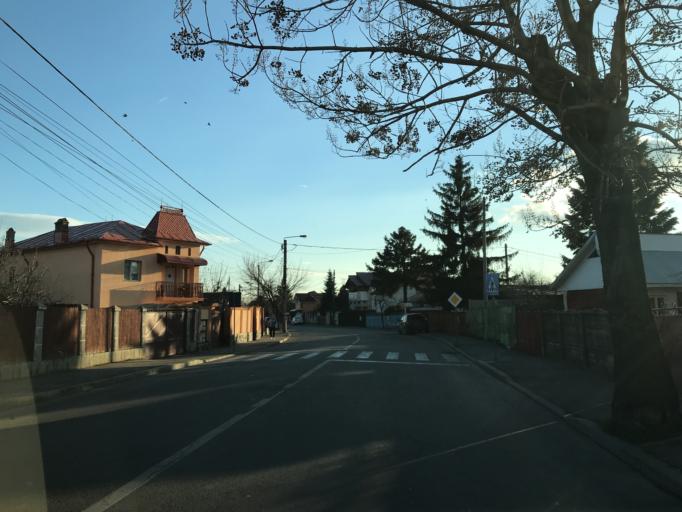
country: RO
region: Olt
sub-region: Municipiul Slatina
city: Slatina
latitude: 44.4220
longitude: 24.3618
